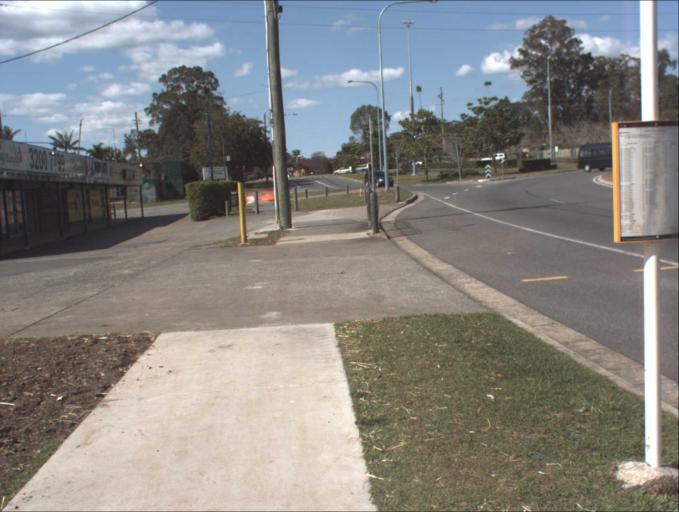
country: AU
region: Queensland
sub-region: Logan
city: Waterford West
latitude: -27.6776
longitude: 153.1200
